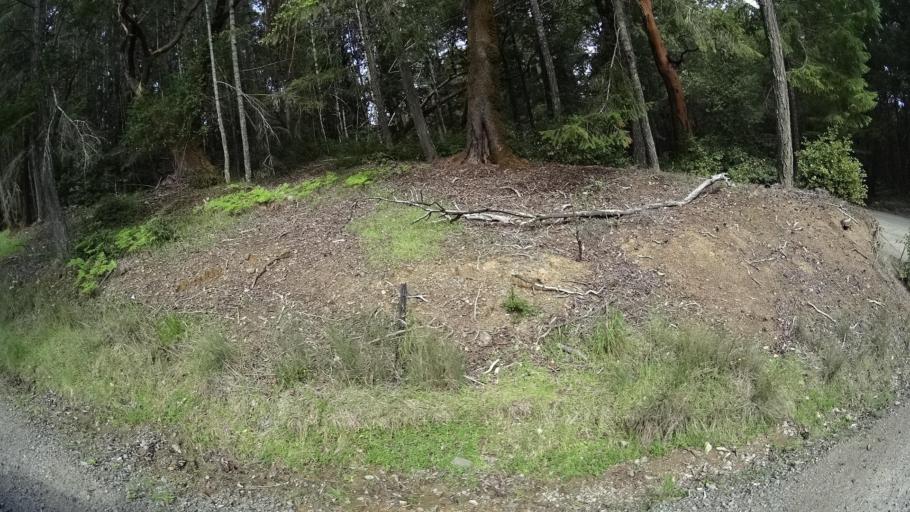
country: US
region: California
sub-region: Humboldt County
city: Redway
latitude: 40.0485
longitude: -123.8361
